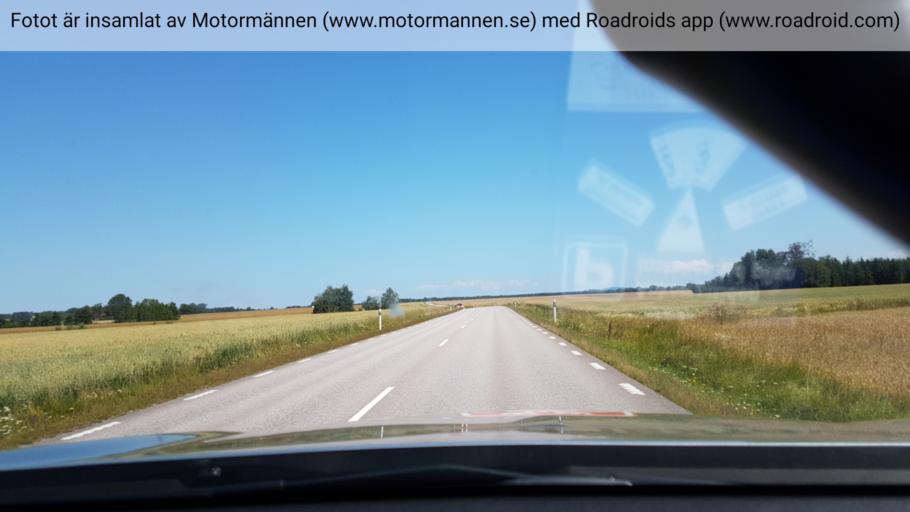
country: SE
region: Vaestra Goetaland
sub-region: Lidkopings Kommun
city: Lidkoping
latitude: 58.4708
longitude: 13.0907
